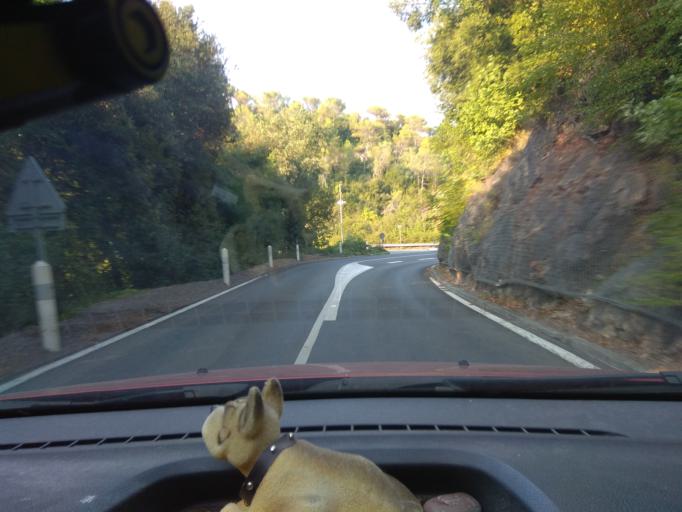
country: FR
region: Provence-Alpes-Cote d'Azur
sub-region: Departement des Alpes-Maritimes
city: Tourrettes-sur-Loup
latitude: 43.6833
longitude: 7.0565
